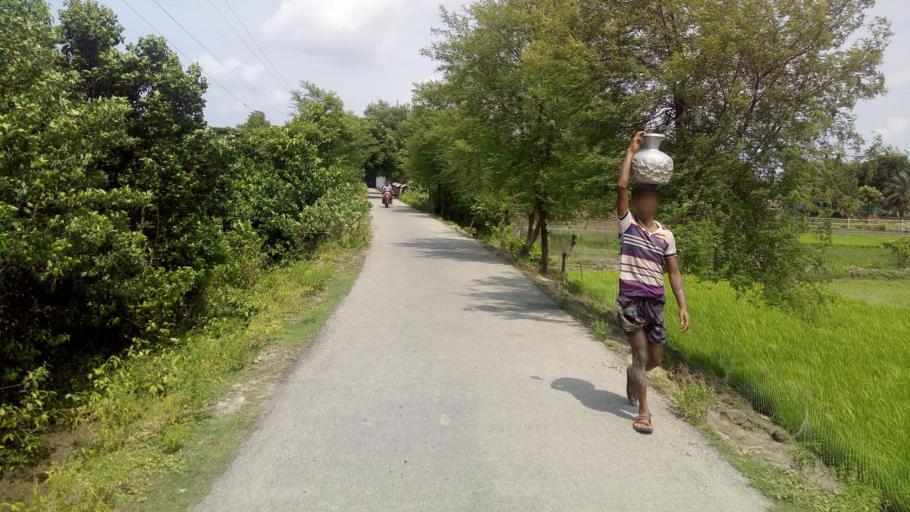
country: BD
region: Khulna
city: Phultala
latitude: 22.5721
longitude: 89.4520
